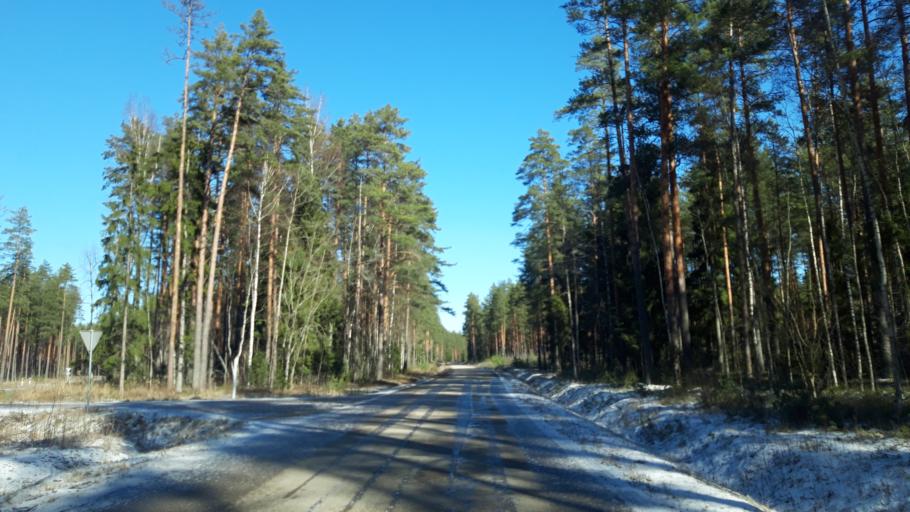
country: LV
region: Strenci
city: Strenci
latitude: 57.5786
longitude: 25.7120
